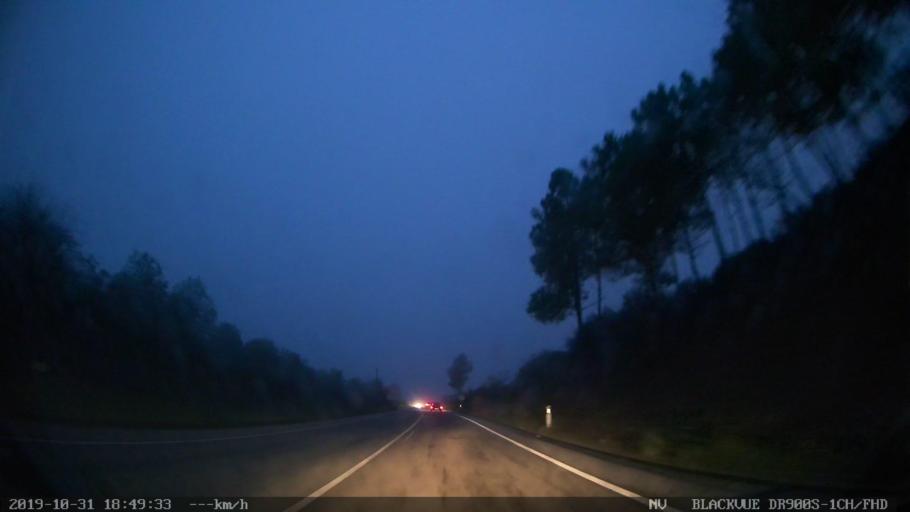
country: PT
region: Vila Real
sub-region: Sabrosa
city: Sabrosa
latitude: 41.2623
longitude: -7.6111
